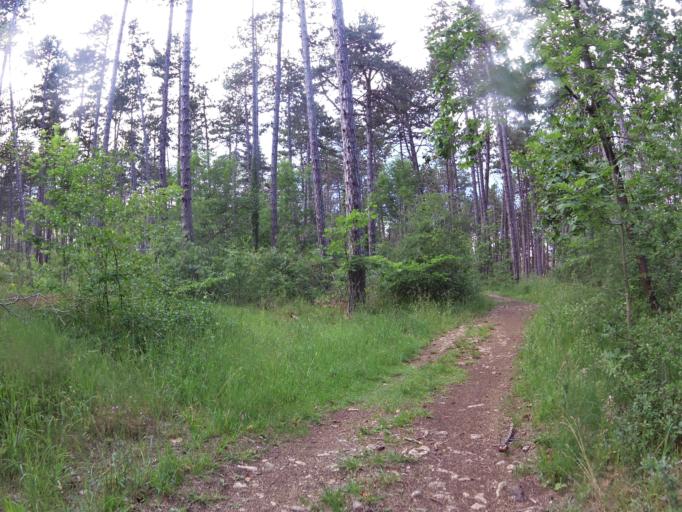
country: DE
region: Bavaria
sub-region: Regierungsbezirk Unterfranken
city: Erlabrunn
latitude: 49.8551
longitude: 9.8364
